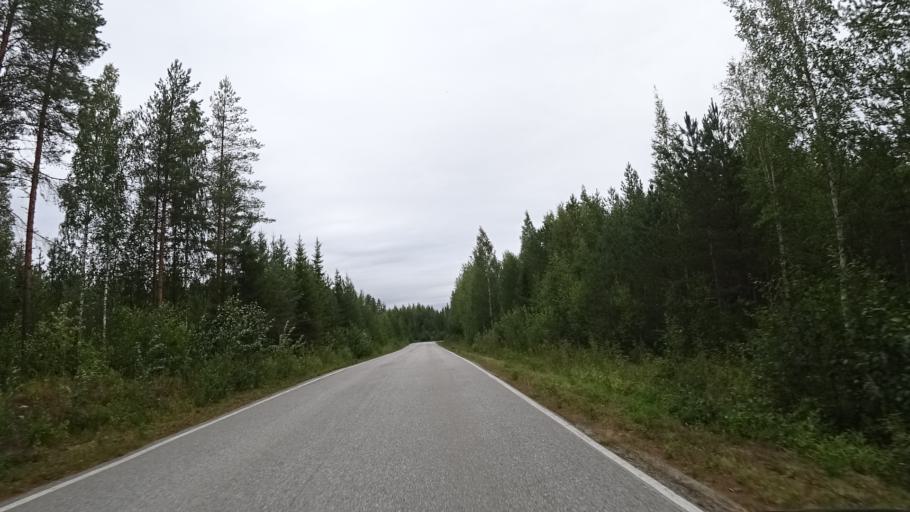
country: FI
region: North Karelia
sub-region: Pielisen Karjala
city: Lieksa
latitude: 63.3556
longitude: 30.2622
